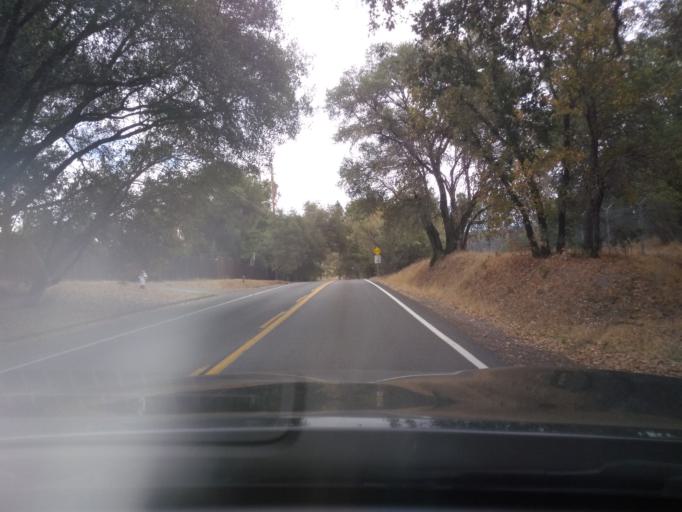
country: US
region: California
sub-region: Mendocino County
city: Ukiah
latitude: 39.1986
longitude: -123.1874
